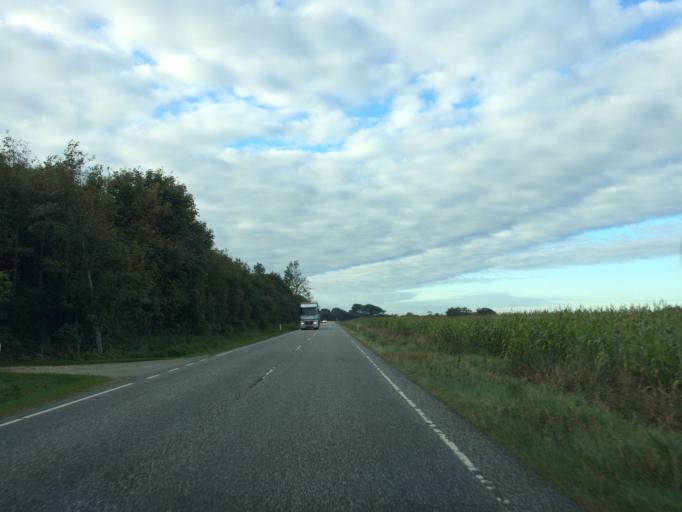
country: DK
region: Central Jutland
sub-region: Ringkobing-Skjern Kommune
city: Skjern
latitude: 55.9795
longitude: 8.5007
